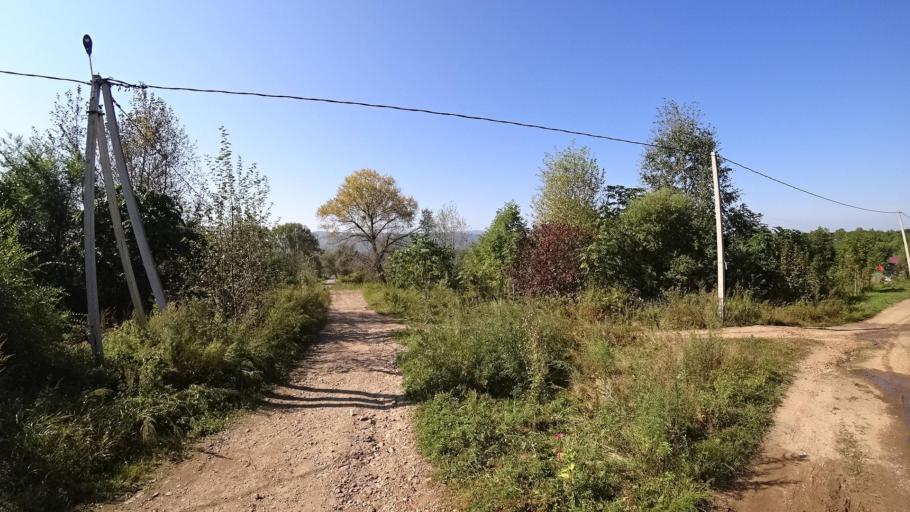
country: RU
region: Jewish Autonomous Oblast
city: Bira
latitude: 49.0056
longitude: 132.4667
